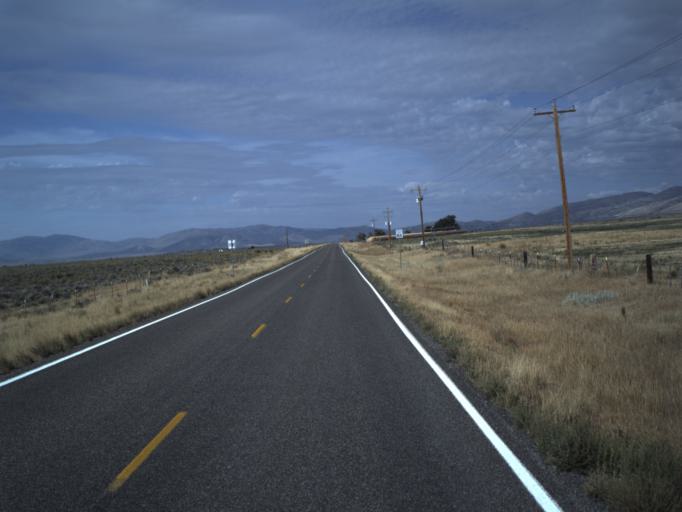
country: US
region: Idaho
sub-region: Cassia County
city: Burley
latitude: 41.8169
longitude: -113.3360
